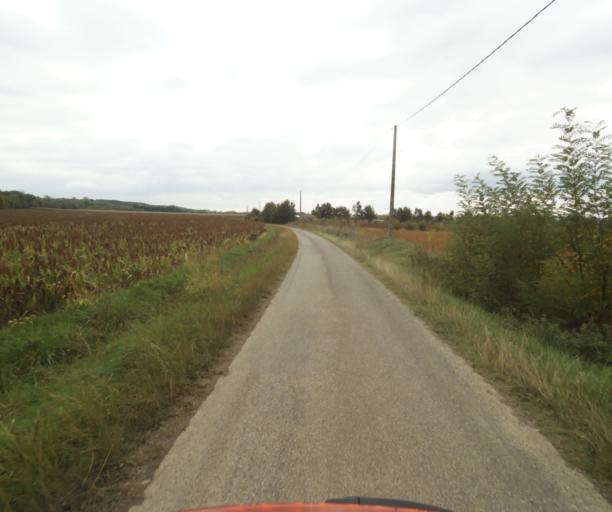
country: FR
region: Midi-Pyrenees
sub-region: Departement du Tarn-et-Garonne
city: Finhan
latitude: 43.9002
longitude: 1.2641
